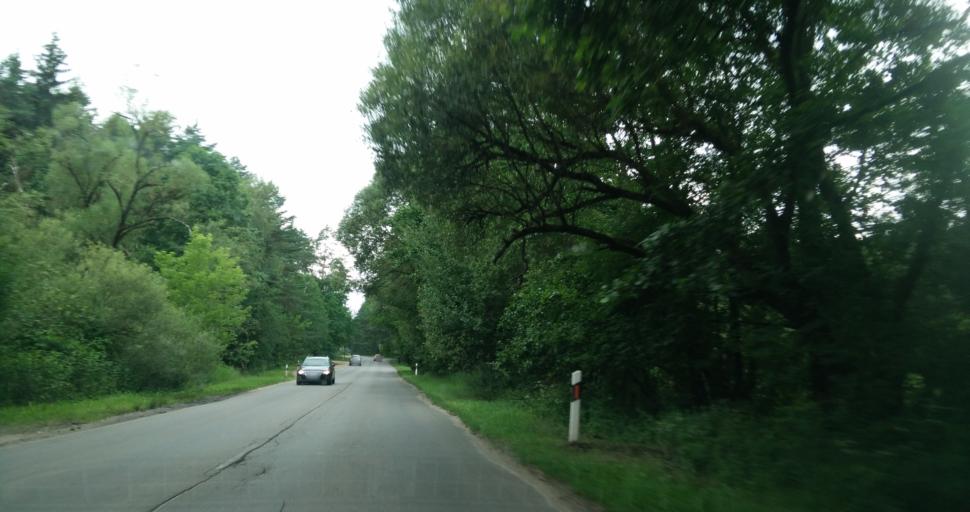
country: LT
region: Vilnius County
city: Rasos
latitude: 54.7340
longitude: 25.3765
